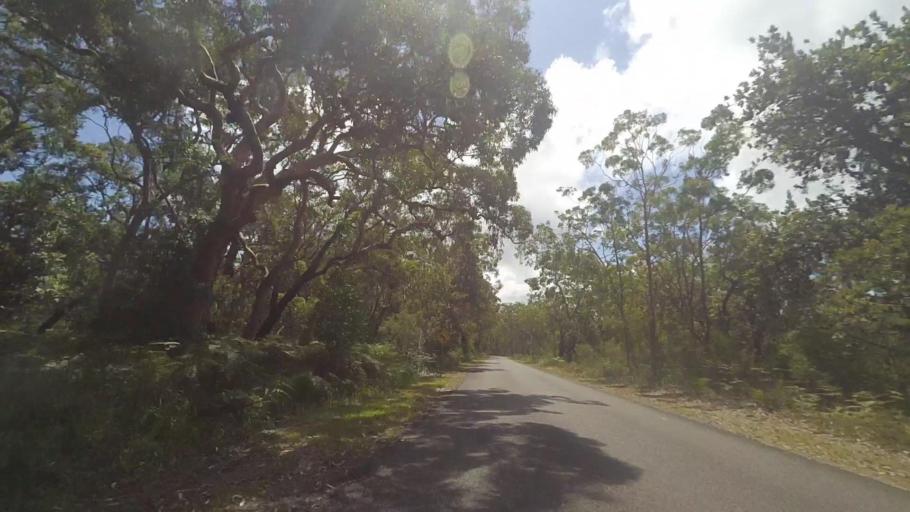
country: AU
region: New South Wales
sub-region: Great Lakes
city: Bulahdelah
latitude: -32.5036
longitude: 152.3101
